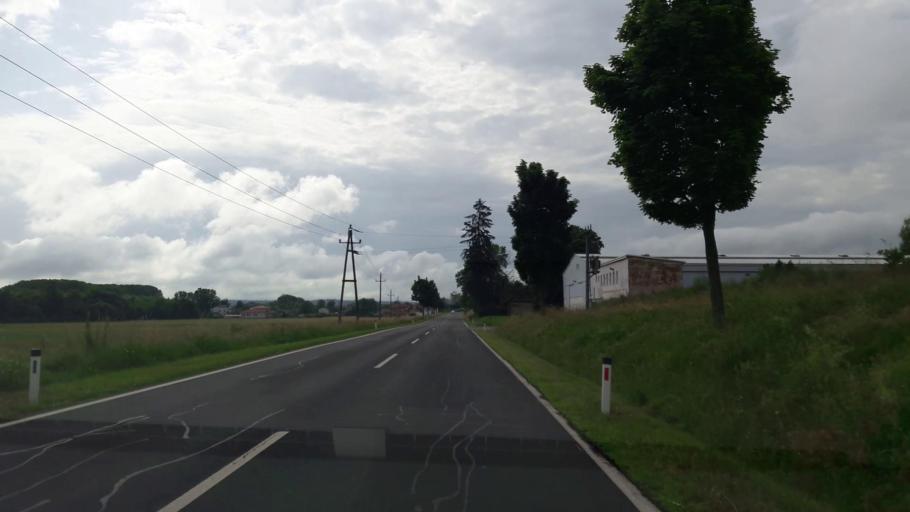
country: AT
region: Burgenland
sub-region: Politischer Bezirk Oberpullendorf
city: Mannersdorf an der Rabnitz
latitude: 47.4678
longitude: 16.5660
